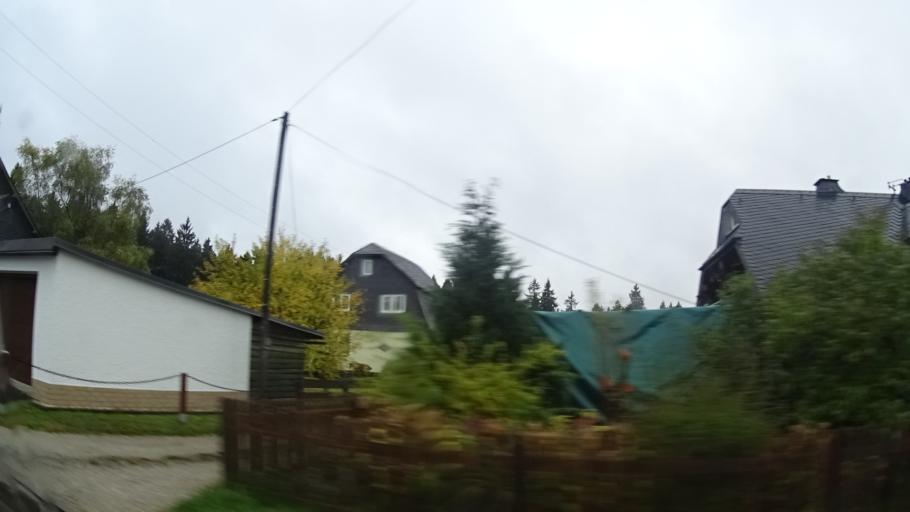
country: DE
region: Bavaria
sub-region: Upper Franconia
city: Tschirn
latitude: 50.4361
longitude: 11.4694
